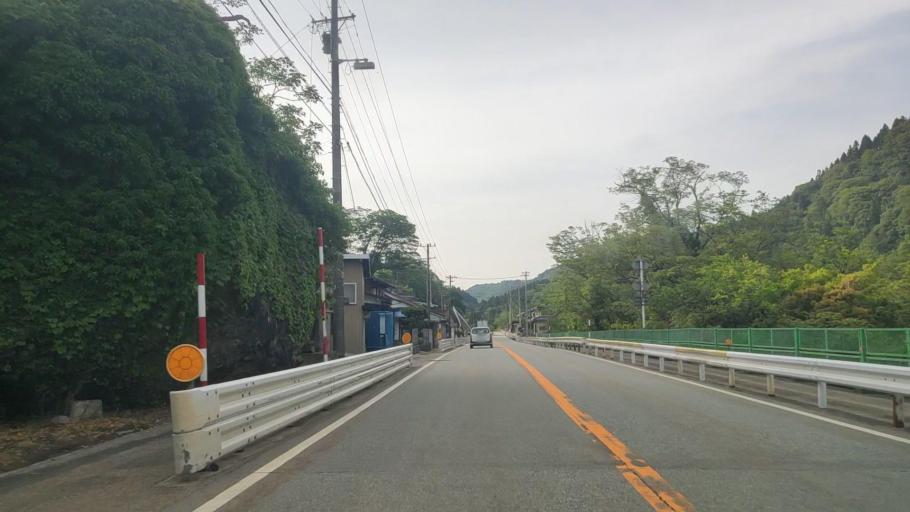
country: JP
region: Toyama
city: Yatsuomachi-higashikumisaka
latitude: 36.4557
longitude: 137.2517
